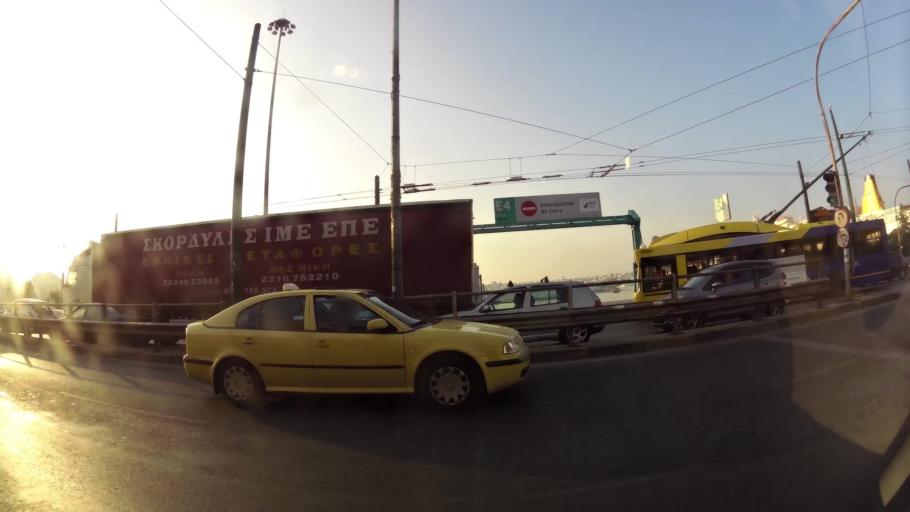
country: GR
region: Attica
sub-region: Nomos Attikis
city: Piraeus
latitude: 37.9494
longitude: 23.6388
